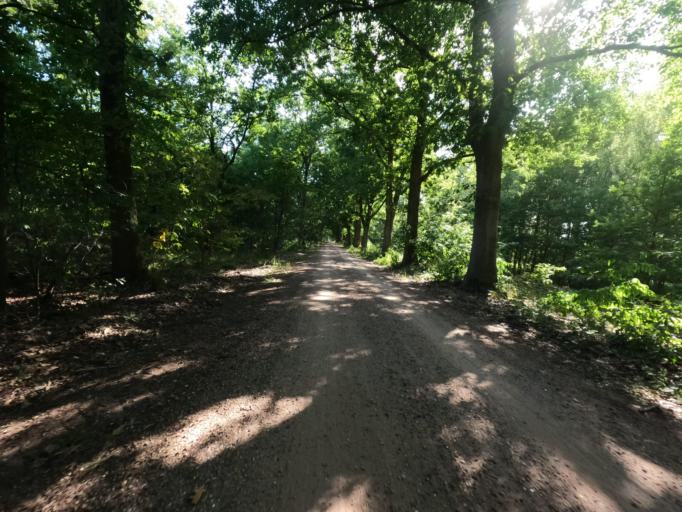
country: NL
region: Limburg
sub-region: Gemeente Beesel
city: Offenbeek
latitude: 51.2585
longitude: 6.1012
